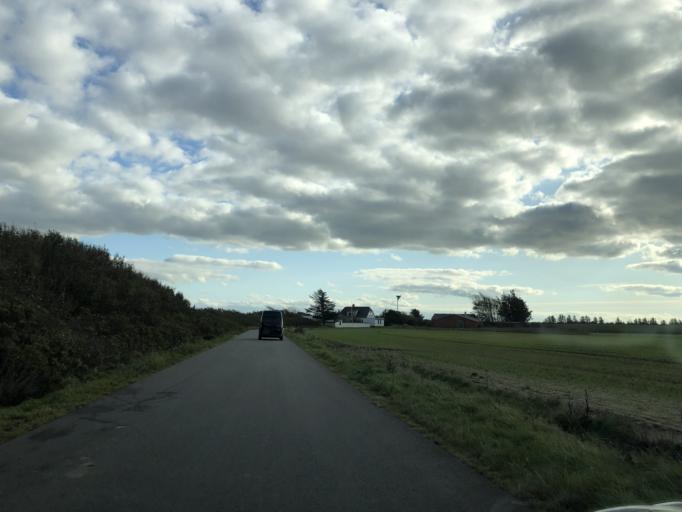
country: DK
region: Central Jutland
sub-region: Holstebro Kommune
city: Ulfborg
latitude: 56.3217
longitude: 8.1574
